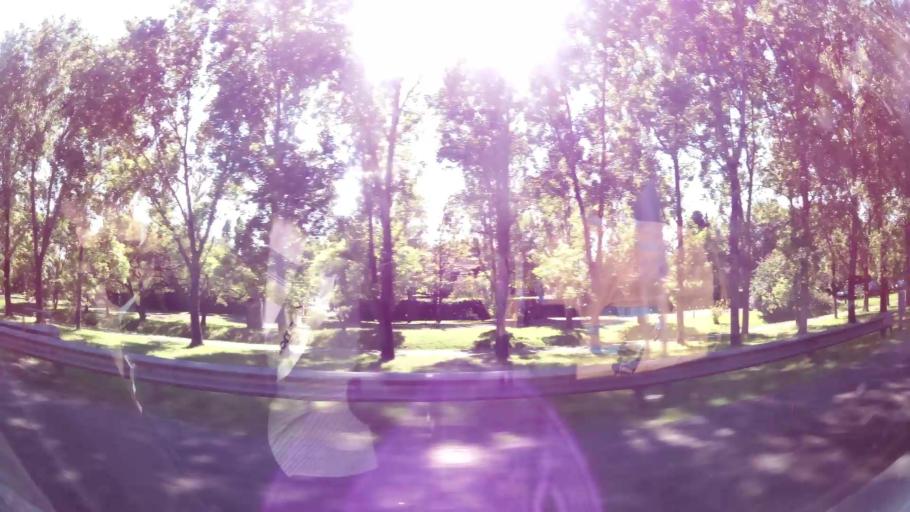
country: AR
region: Buenos Aires
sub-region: Partido de San Isidro
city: San Isidro
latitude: -34.4816
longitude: -58.5614
